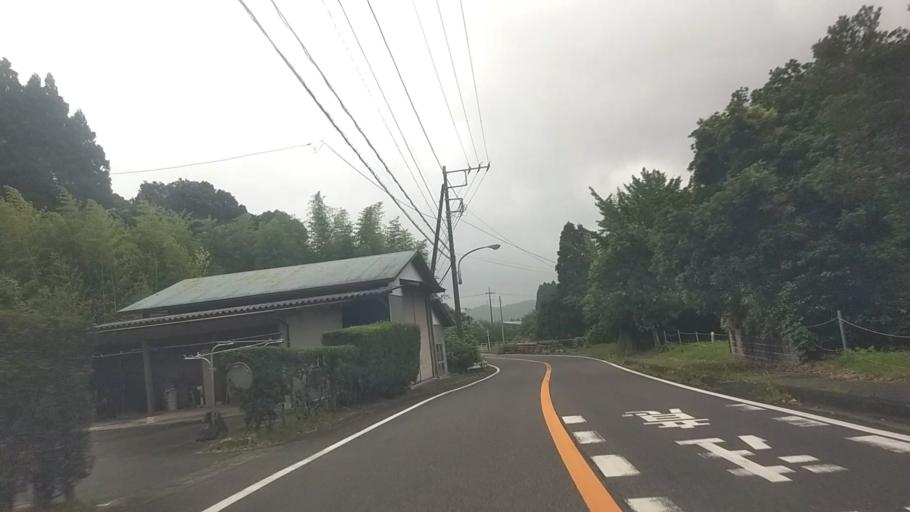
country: JP
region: Chiba
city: Katsuura
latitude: 35.2533
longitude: 140.2242
